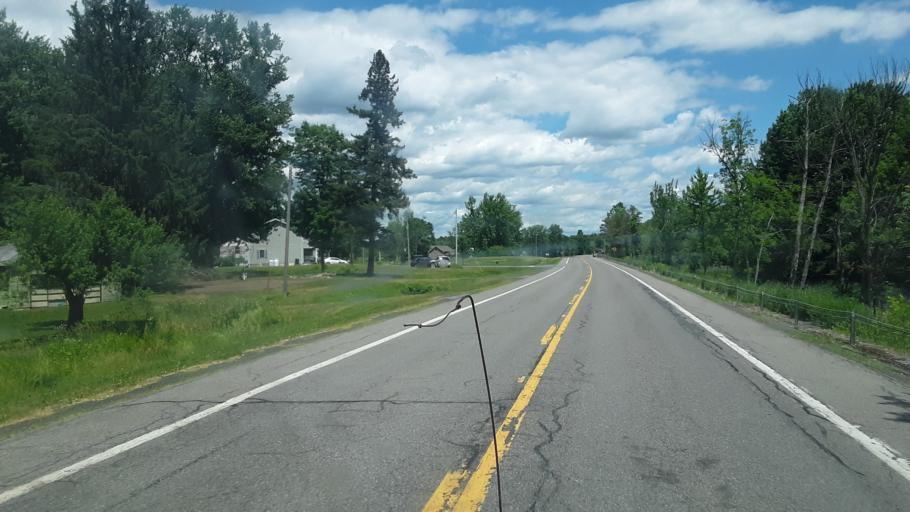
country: US
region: New York
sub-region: Madison County
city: Oneida
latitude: 43.1916
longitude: -75.6232
